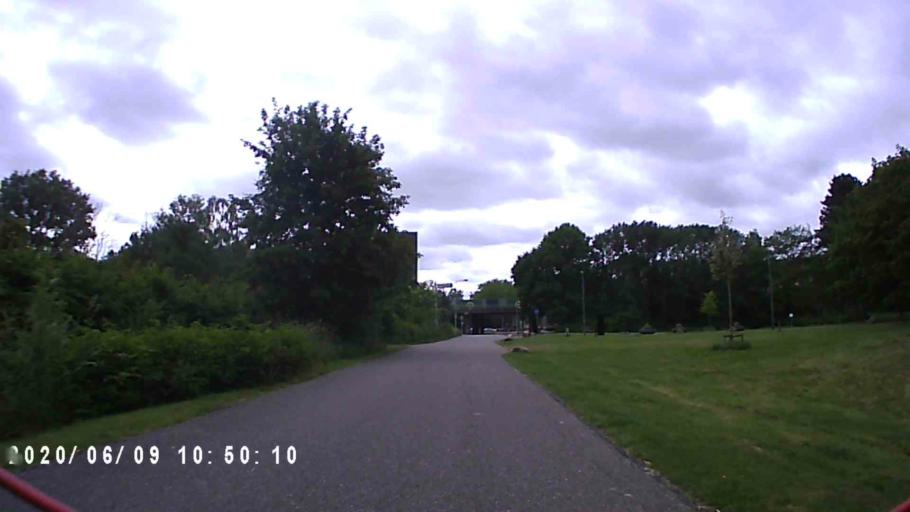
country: NL
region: Groningen
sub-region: Gemeente Groningen
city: Korrewegwijk
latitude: 53.2394
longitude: 6.5543
